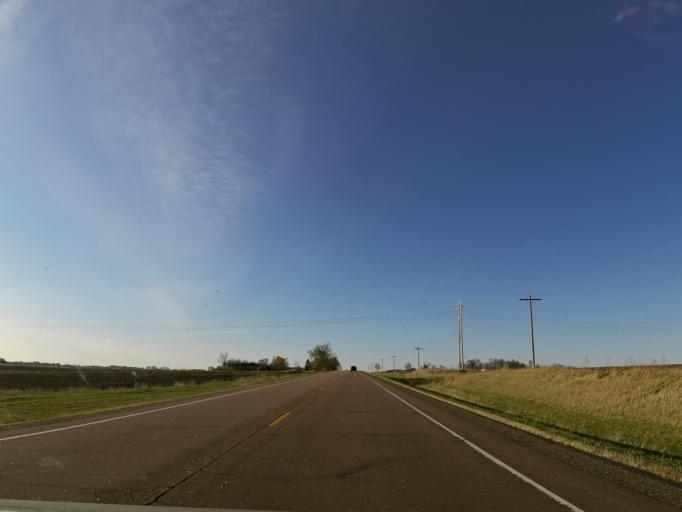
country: US
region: Minnesota
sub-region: Goodhue County
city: Cannon Falls
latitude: 44.5491
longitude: -92.9947
